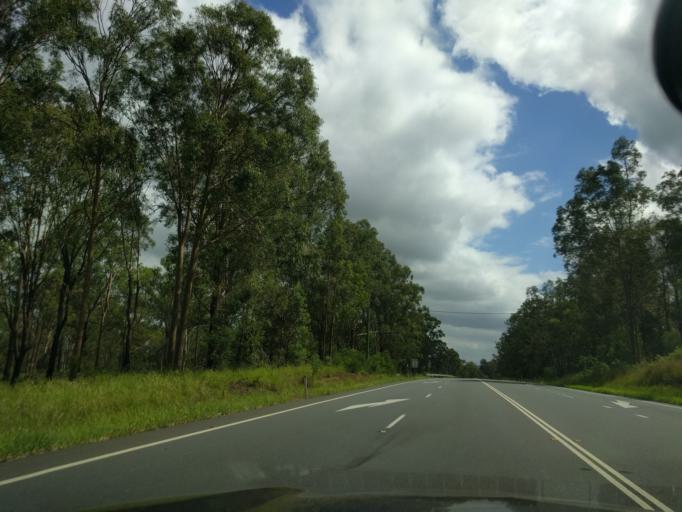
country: AU
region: Queensland
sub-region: Logan
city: Cedar Vale
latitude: -27.8784
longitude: 152.9898
